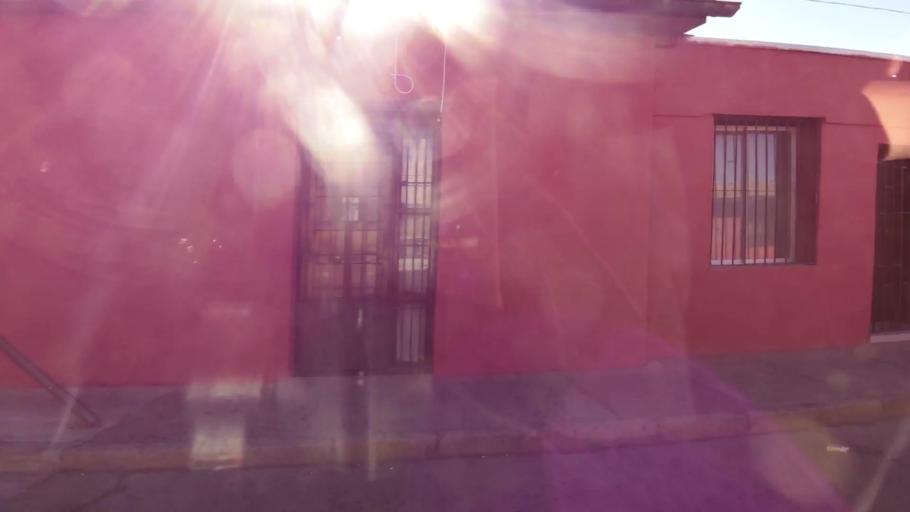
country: CL
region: O'Higgins
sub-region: Provincia de Cachapoal
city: Rancagua
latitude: -34.1677
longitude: -70.7360
